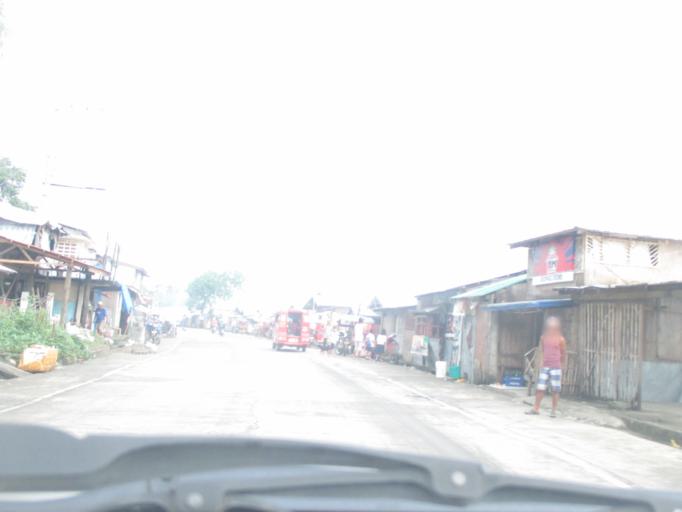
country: PH
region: Eastern Visayas
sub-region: Province of Leyte
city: Panalanoy
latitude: 11.2488
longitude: 124.9938
